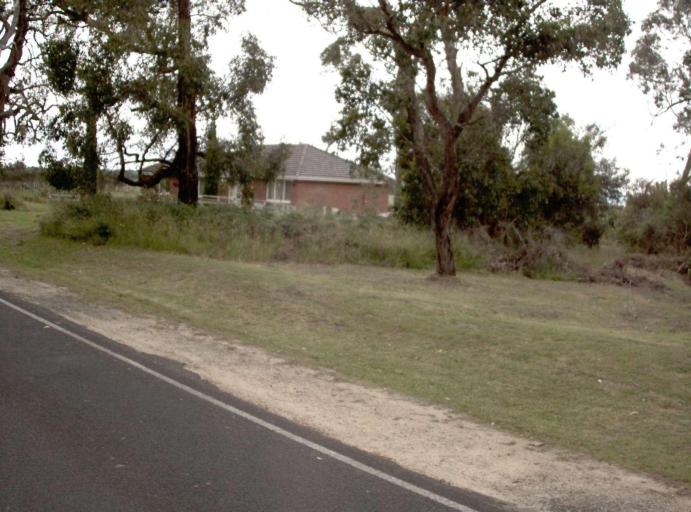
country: AU
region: Victoria
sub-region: Bass Coast
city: North Wonthaggi
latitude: -38.4300
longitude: 145.4840
